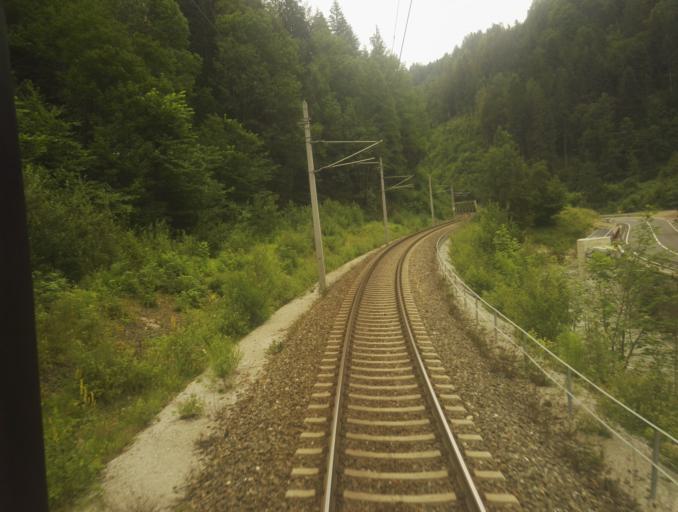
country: AT
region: Salzburg
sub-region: Politischer Bezirk Sankt Johann im Pongau
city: Huttau
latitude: 47.4278
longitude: 13.2807
